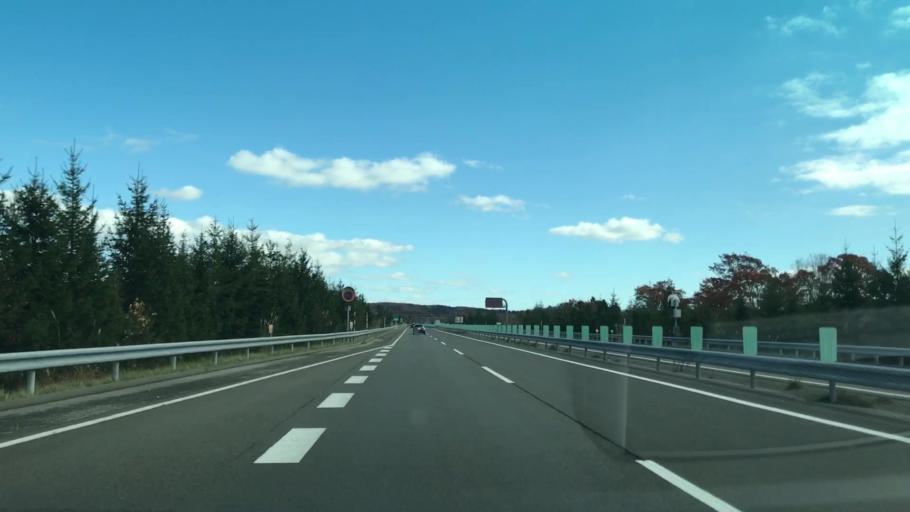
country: JP
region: Hokkaido
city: Chitose
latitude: 42.8812
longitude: 141.7156
